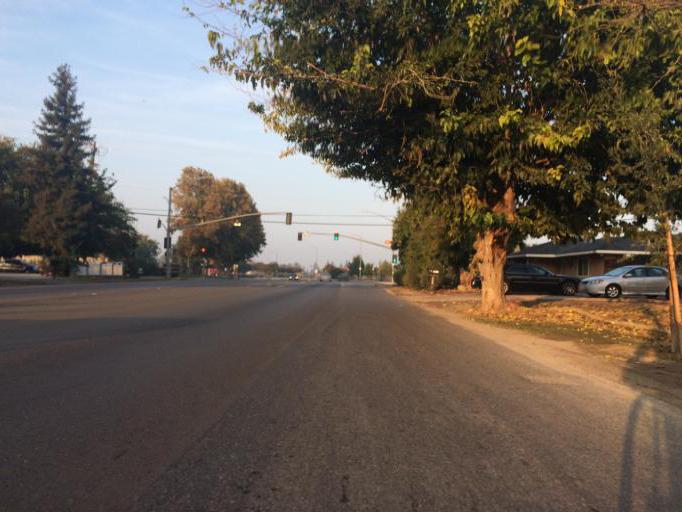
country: US
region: California
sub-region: Fresno County
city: Tarpey Village
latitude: 36.7945
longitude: -119.7084
